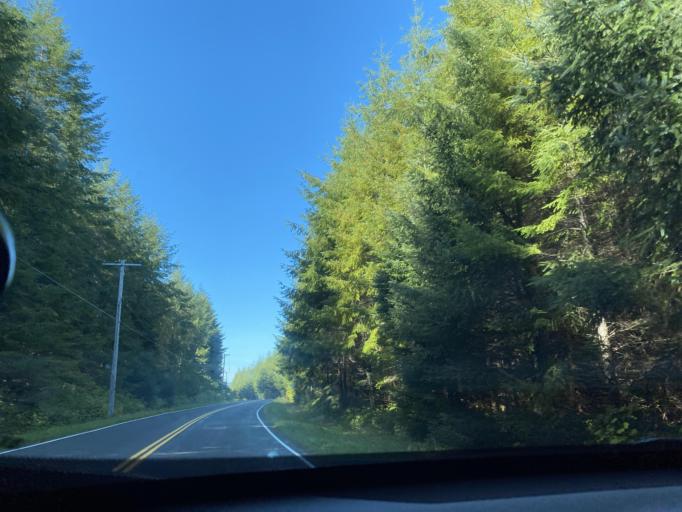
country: US
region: Washington
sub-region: Clallam County
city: Forks
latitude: 47.9470
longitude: -124.4861
